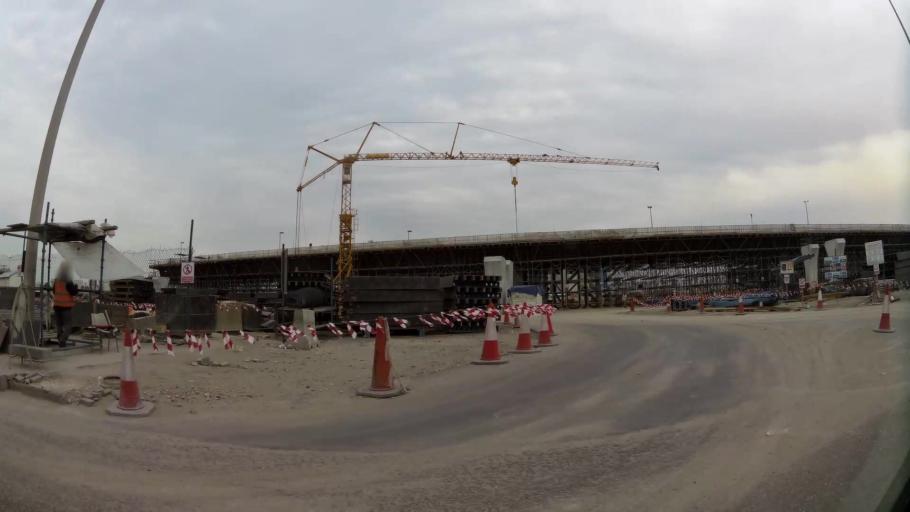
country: BH
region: Northern
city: Sitrah
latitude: 26.1310
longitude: 50.6005
